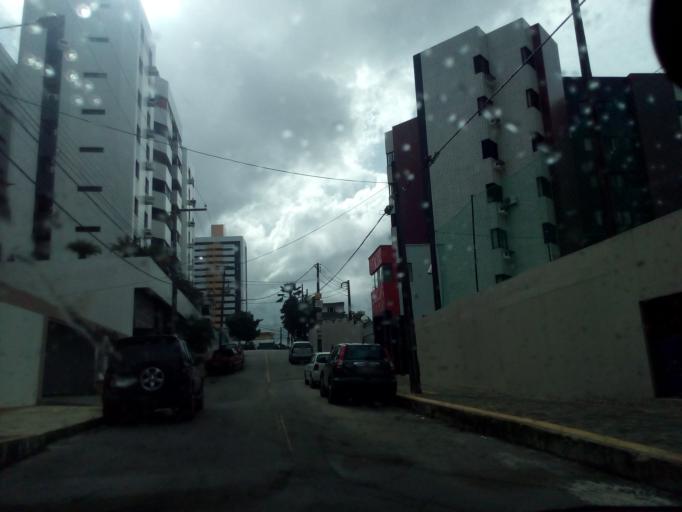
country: BR
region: Rio Grande do Norte
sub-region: Natal
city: Natal
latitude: -5.8019
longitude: -35.2080
